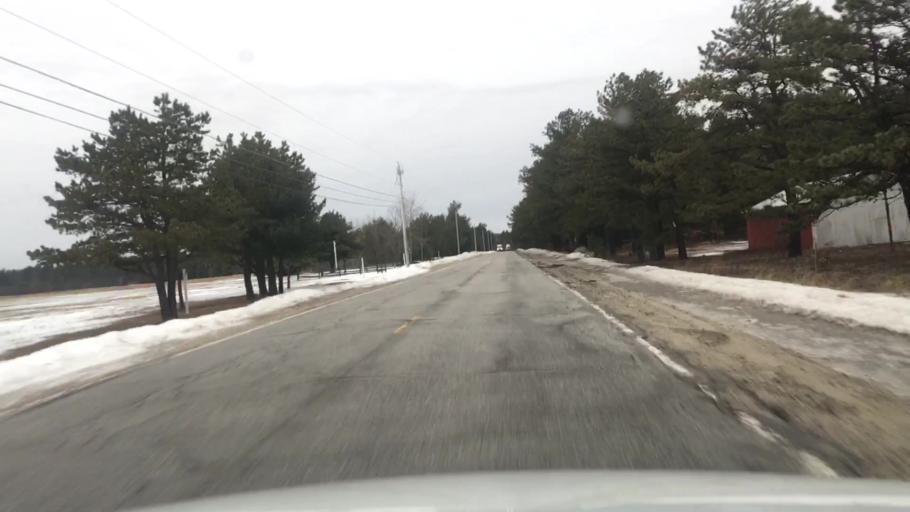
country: US
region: Maine
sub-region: York County
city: Shapleigh
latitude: 43.5904
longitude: -70.8776
